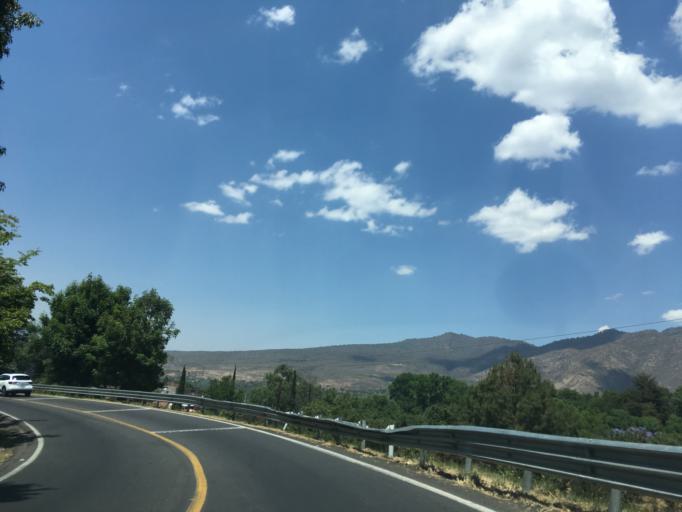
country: MX
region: Michoacan
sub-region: Chilchota
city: Tacuro (Santa Maria Tacuro)
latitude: 19.8513
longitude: -102.0307
